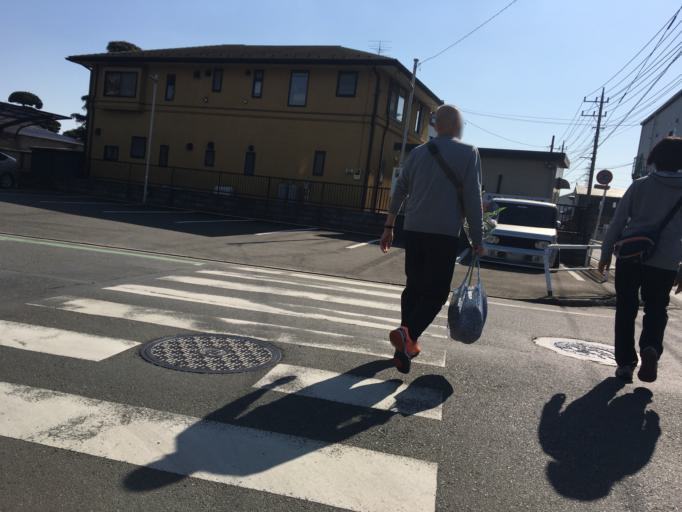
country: JP
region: Saitama
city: Oi
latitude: 35.8482
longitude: 139.5203
